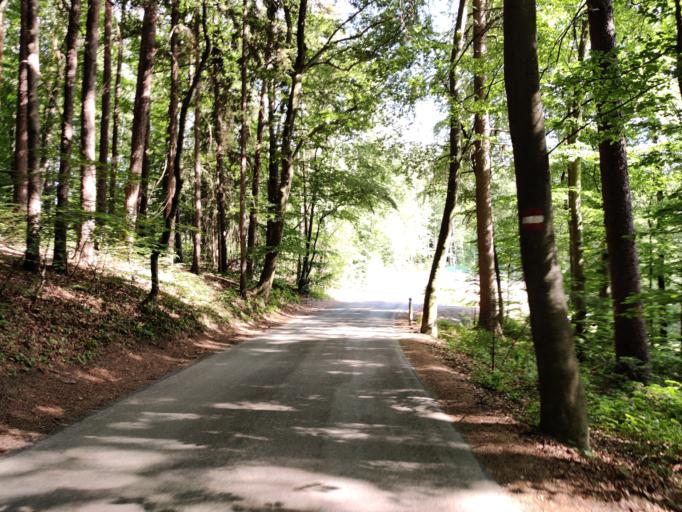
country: AT
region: Styria
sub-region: Politischer Bezirk Graz-Umgebung
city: Pirka
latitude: 47.0329
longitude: 15.3688
